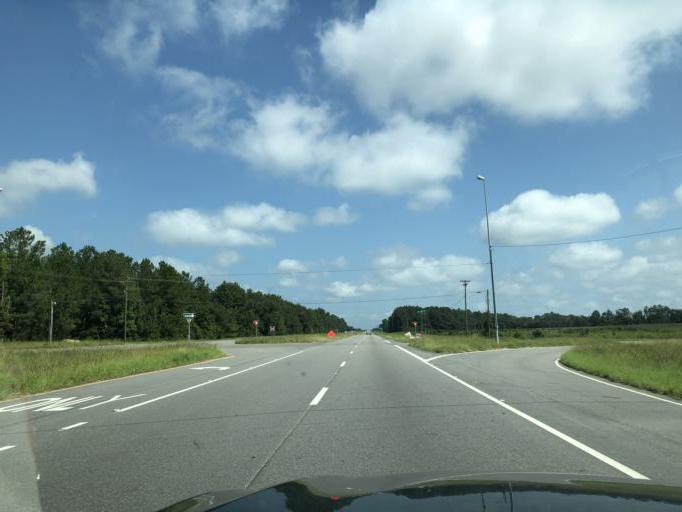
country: US
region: Alabama
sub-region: Houston County
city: Rehobeth
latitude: 31.0337
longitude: -85.4065
